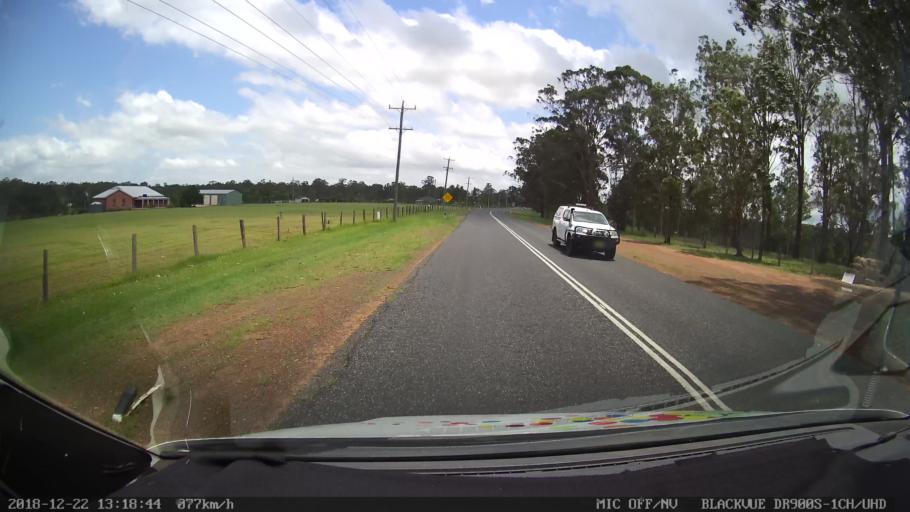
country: AU
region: New South Wales
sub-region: Clarence Valley
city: South Grafton
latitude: -29.7497
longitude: 152.9328
